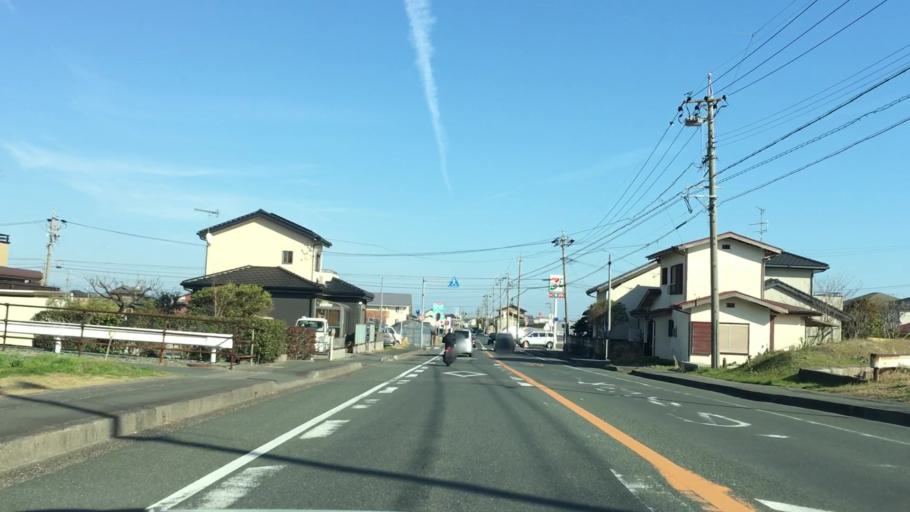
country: JP
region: Shizuoka
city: Kosai-shi
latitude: 34.7005
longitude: 137.6178
